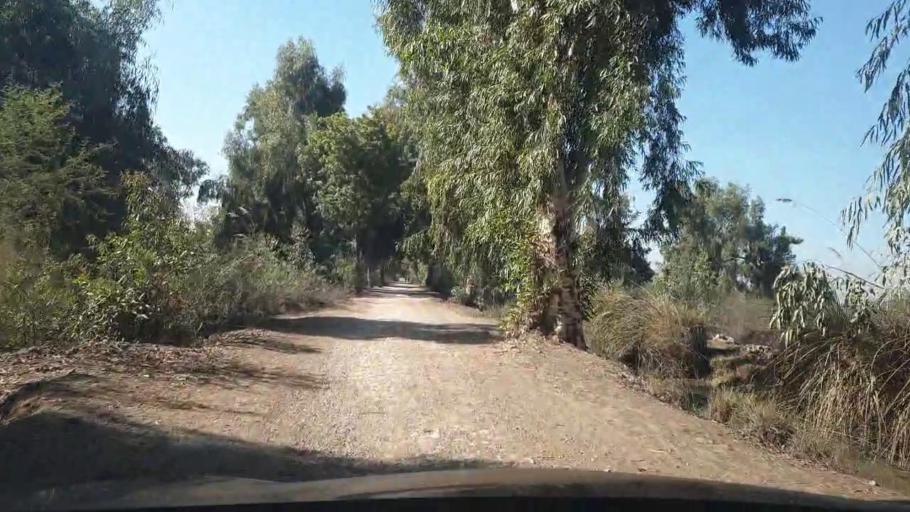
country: PK
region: Sindh
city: Mirpur Mathelo
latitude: 28.0592
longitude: 69.5067
